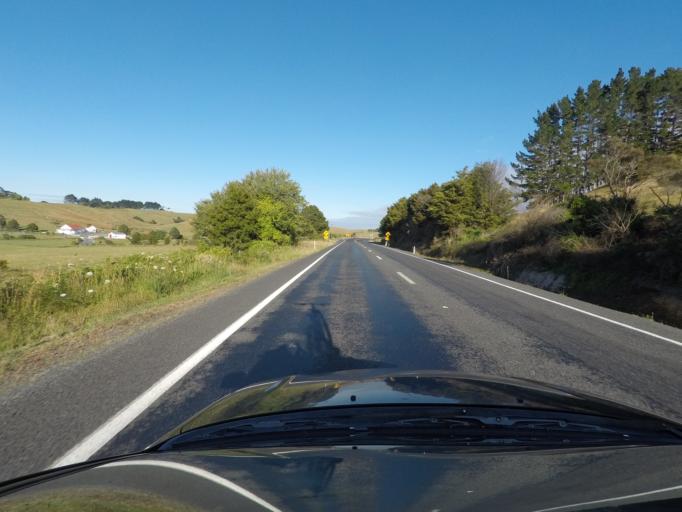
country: NZ
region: Northland
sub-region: Far North District
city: Kawakawa
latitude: -35.4933
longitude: 174.1360
